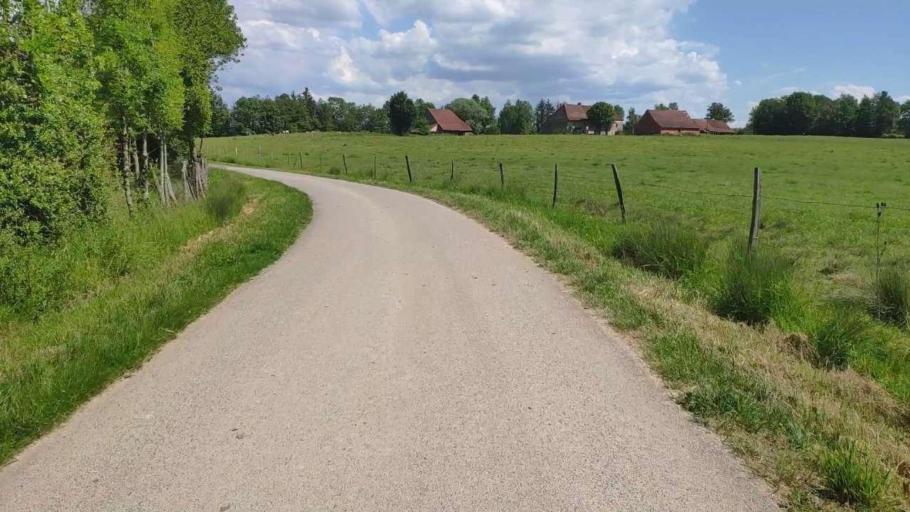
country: FR
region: Franche-Comte
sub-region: Departement du Jura
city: Bletterans
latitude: 46.7983
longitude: 5.4127
